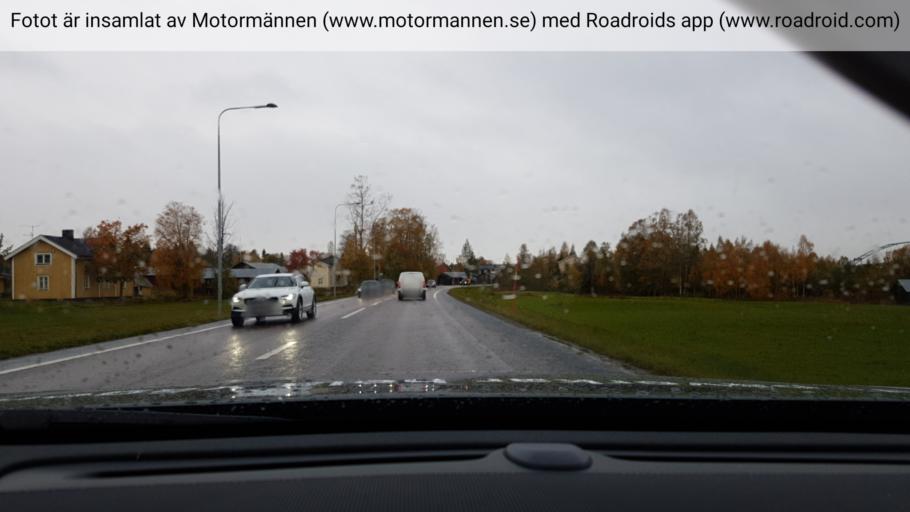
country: SE
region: Norrbotten
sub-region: Lulea Kommun
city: Gammelstad
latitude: 65.5842
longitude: 22.0332
